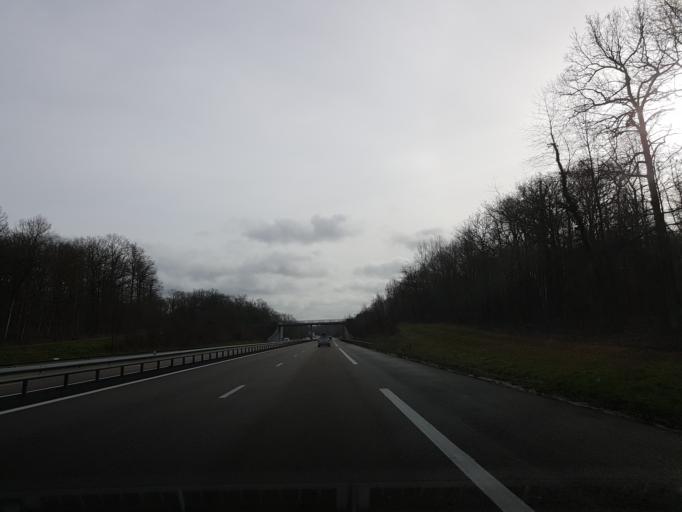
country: FR
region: Champagne-Ardenne
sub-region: Departement de l'Aube
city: Lusigny-sur-Barse
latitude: 48.1911
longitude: 4.2750
